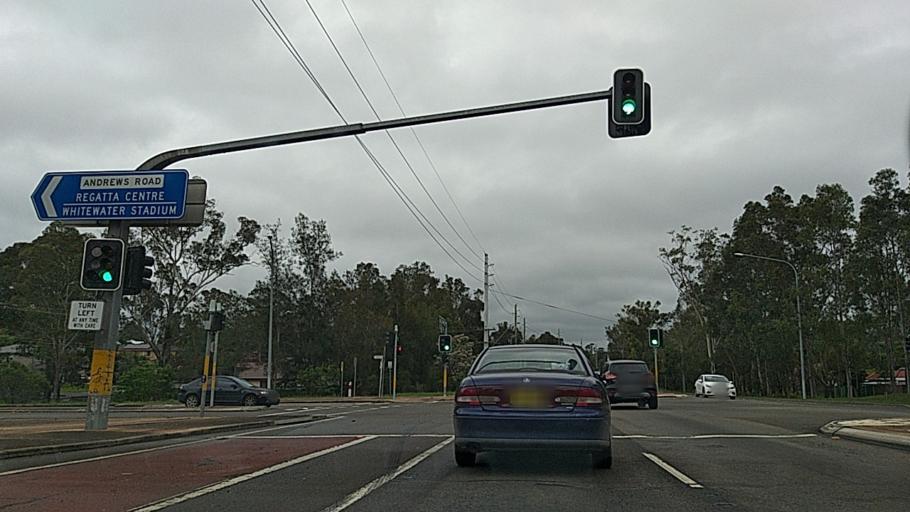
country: AU
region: New South Wales
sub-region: Penrith Municipality
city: Werrington Downs
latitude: -33.7353
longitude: 150.7174
